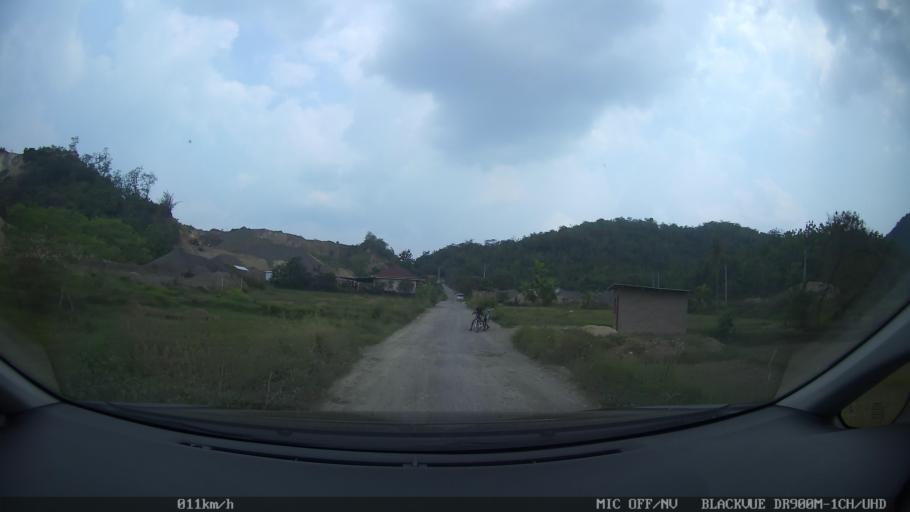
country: ID
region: Lampung
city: Gadingrejo
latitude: -5.3839
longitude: 105.0349
